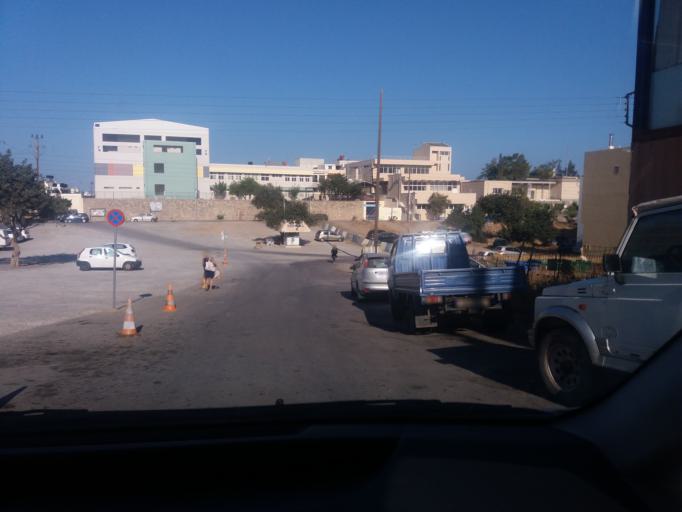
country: GR
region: Crete
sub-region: Nomos Lasithiou
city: Agios Nikolaos
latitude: 35.1936
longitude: 25.7136
